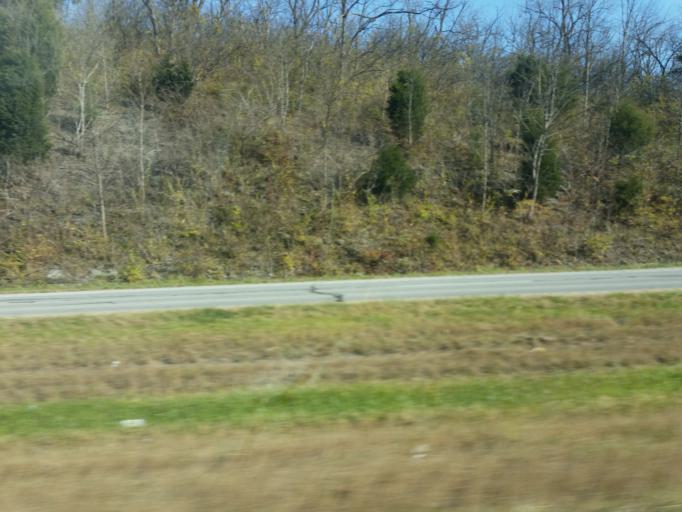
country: US
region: Ohio
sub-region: Hamilton County
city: Dunlap
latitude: 39.2758
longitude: -84.6043
